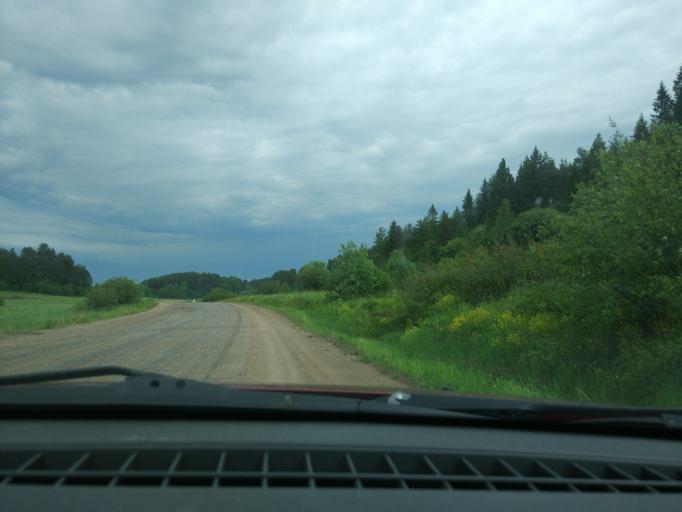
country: RU
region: Leningrad
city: Kuznechnoye
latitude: 61.2765
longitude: 29.8475
